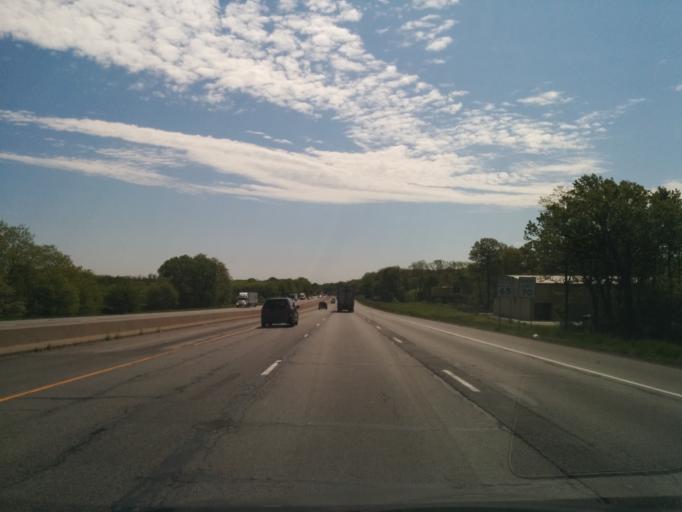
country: US
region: Indiana
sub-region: Porter County
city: Portage
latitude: 41.6017
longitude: -87.1613
